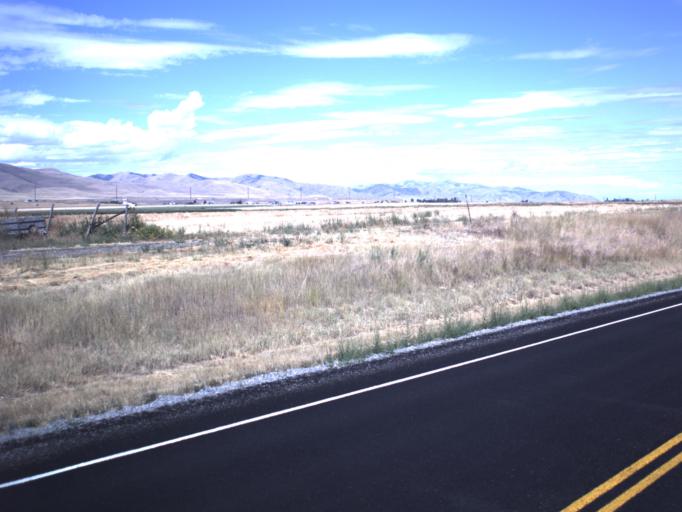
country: US
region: Utah
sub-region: Box Elder County
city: Garland
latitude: 41.8291
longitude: -112.1456
